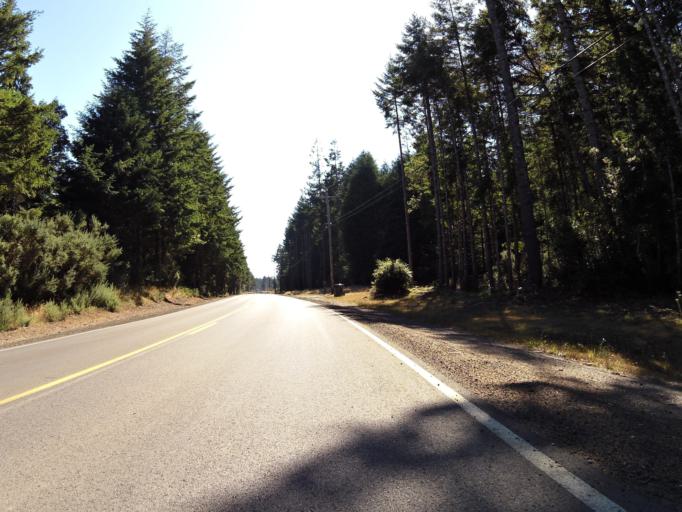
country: US
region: Oregon
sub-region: Coos County
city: Bandon
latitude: 43.1927
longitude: -124.3674
